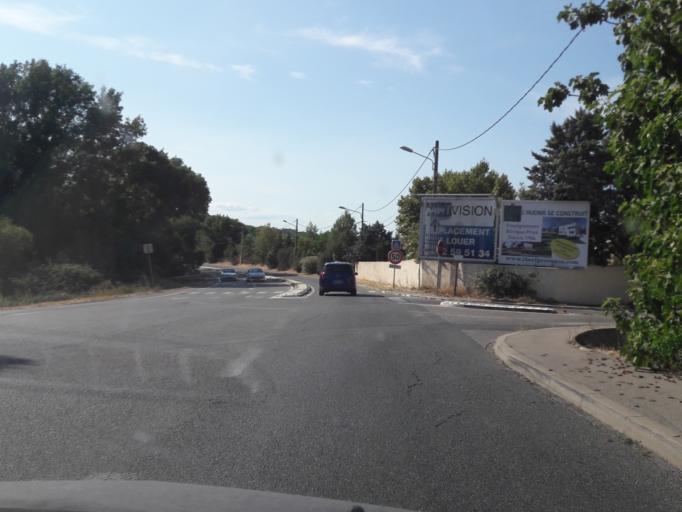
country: FR
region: Provence-Alpes-Cote d'Azur
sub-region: Departement des Bouches-du-Rhone
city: Bouc-Bel-Air
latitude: 43.4800
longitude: 5.4235
